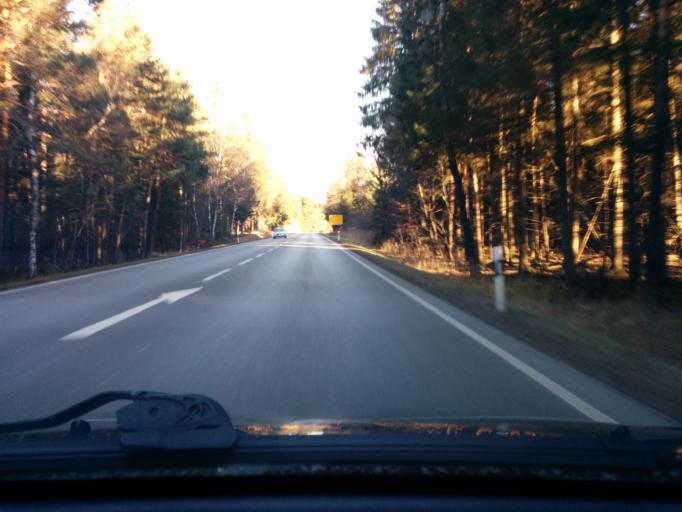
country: DE
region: Bavaria
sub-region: Upper Bavaria
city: Pahl
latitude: 47.9146
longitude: 11.2224
